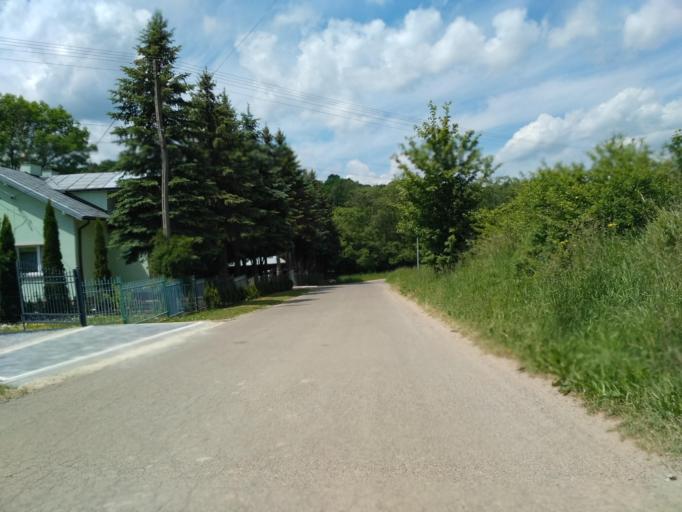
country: PL
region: Subcarpathian Voivodeship
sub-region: Powiat krosnienski
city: Dukla
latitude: 49.5849
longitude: 21.6235
